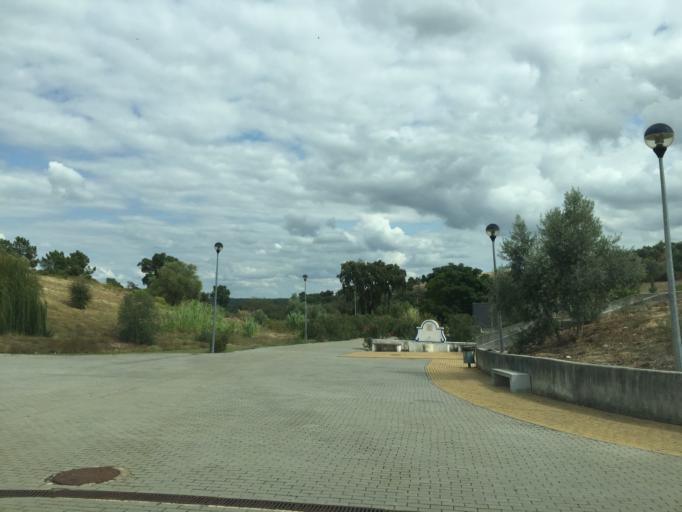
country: PT
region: Portalegre
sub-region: Ponte de Sor
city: Santo Andre
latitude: 39.0812
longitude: -8.1726
